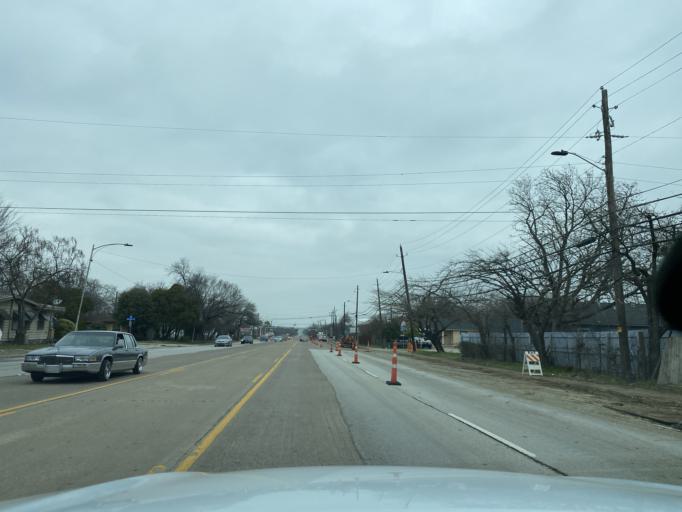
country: US
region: Texas
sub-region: Tarrant County
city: Arlington
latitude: 32.7186
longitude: -97.0974
